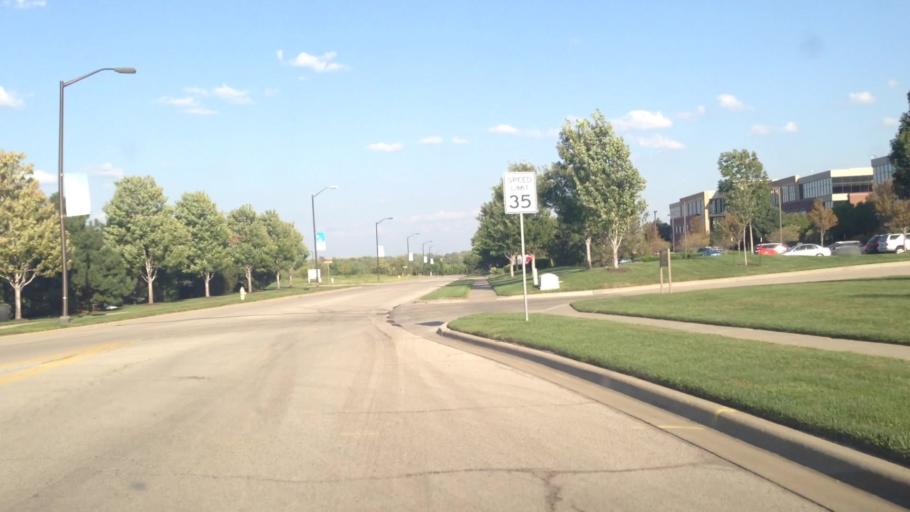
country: US
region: Kansas
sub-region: Johnson County
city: Olathe
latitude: 38.9362
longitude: -94.7964
